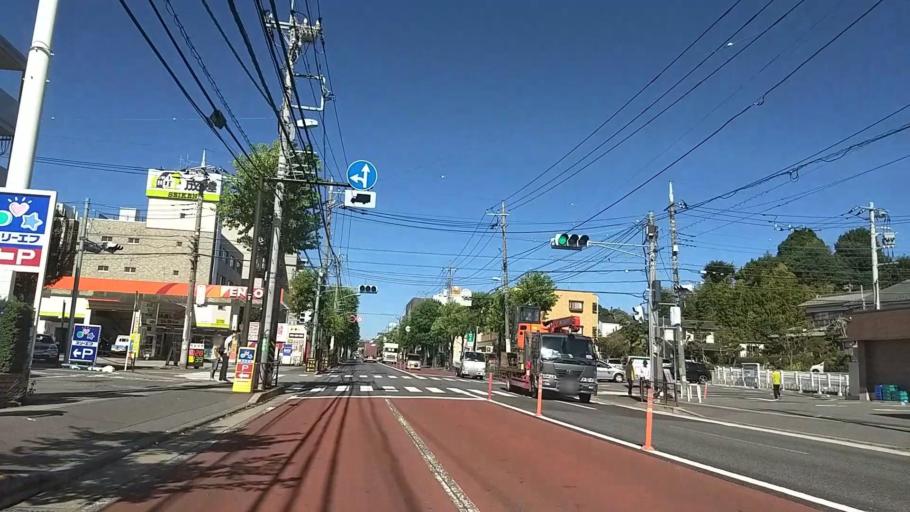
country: JP
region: Tokyo
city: Chofugaoka
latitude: 35.5853
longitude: 139.5787
